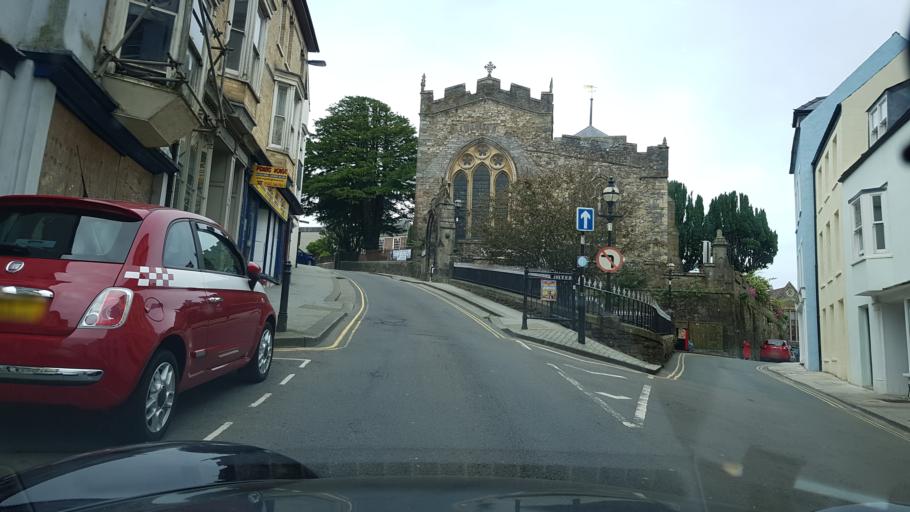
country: GB
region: Wales
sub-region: Pembrokeshire
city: Haverfordwest
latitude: 51.8013
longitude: -4.9709
